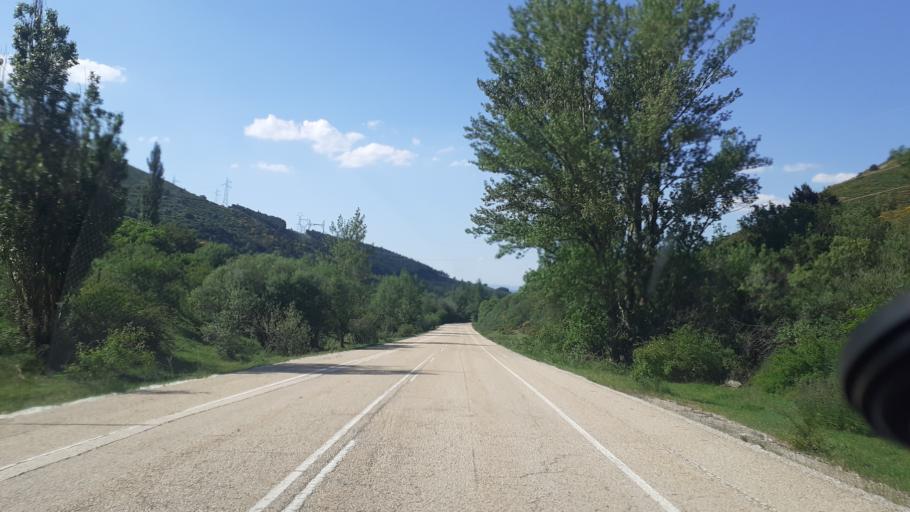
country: ES
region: Madrid
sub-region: Provincia de Madrid
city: Somosierra
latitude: 41.1500
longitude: -3.5820
